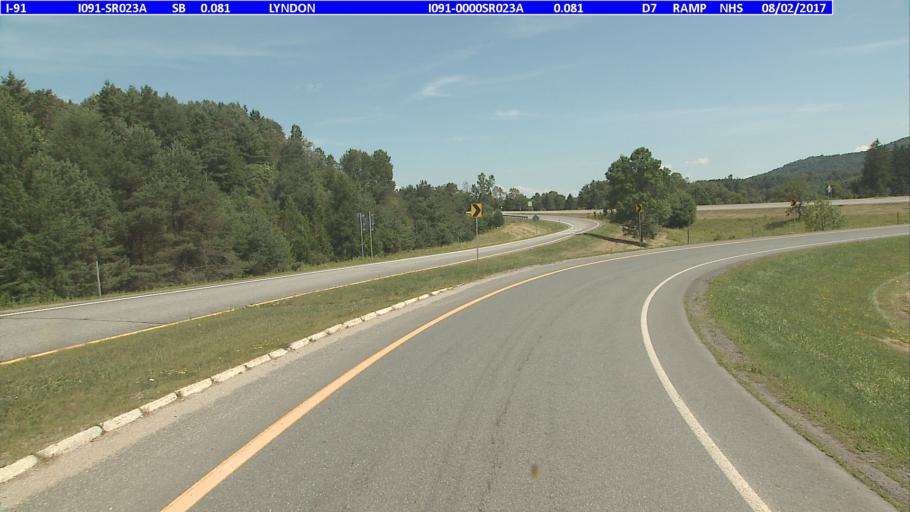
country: US
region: Vermont
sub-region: Caledonia County
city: Lyndon
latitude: 44.5173
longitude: -72.0088
